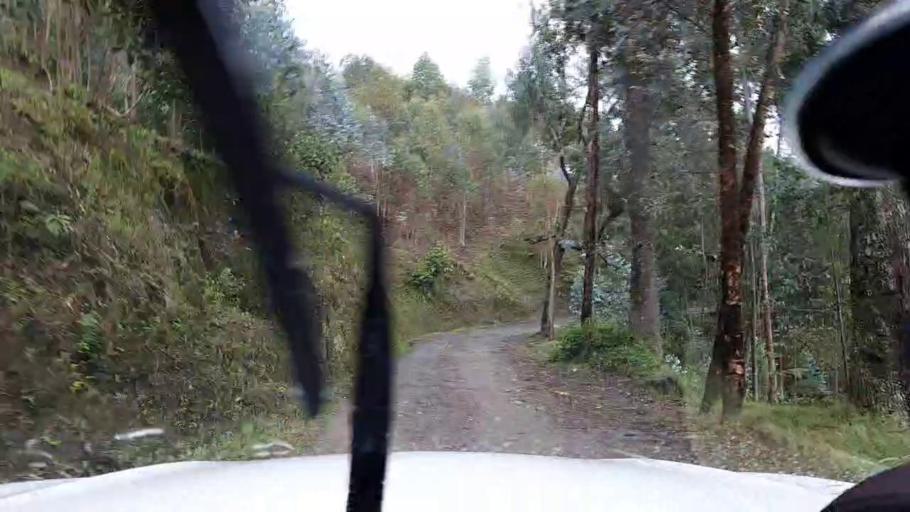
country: RW
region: Western Province
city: Kibuye
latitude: -2.0759
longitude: 29.5135
